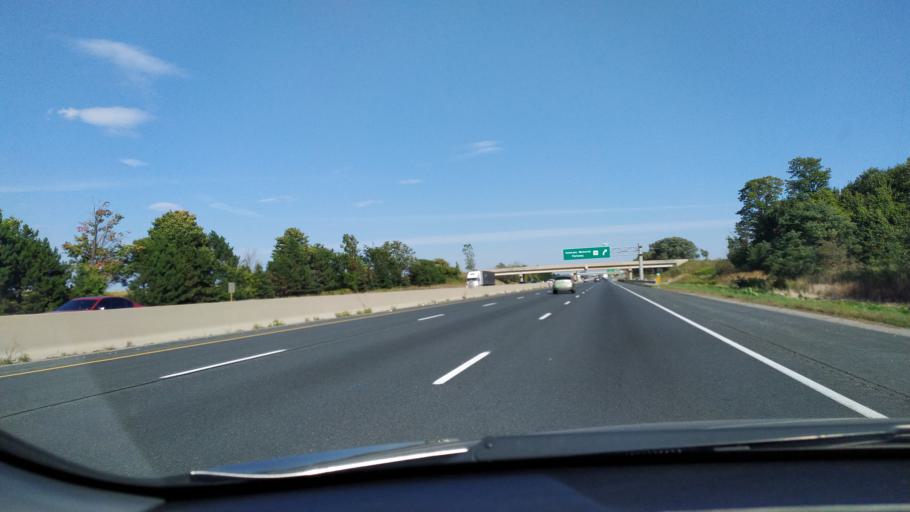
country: CA
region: Ontario
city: Dorchester
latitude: 42.9417
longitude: -81.1389
